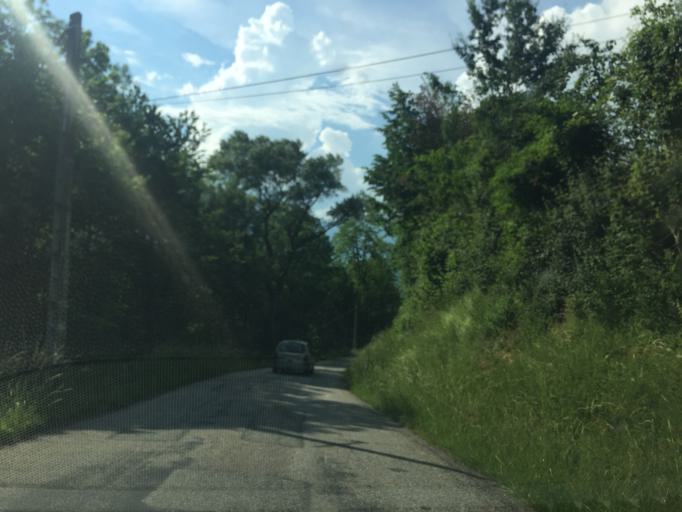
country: FR
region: Rhone-Alpes
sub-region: Departement de la Savoie
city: Aiton
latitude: 45.5333
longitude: 6.3235
